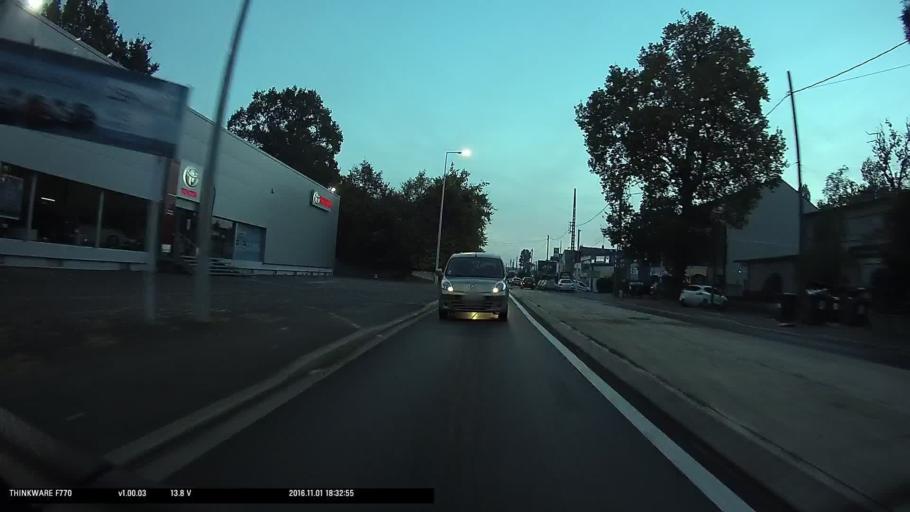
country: FR
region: Ile-de-France
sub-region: Departement de l'Essonne
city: Villemoisson-sur-Orge
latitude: 48.6543
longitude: 2.3382
